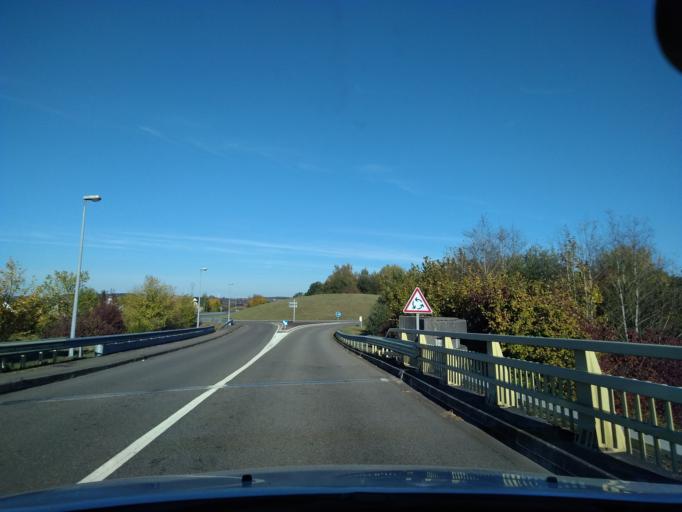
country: FR
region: Lorraine
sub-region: Departement de la Moselle
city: Sarreguemines
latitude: 49.1188
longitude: 7.0330
